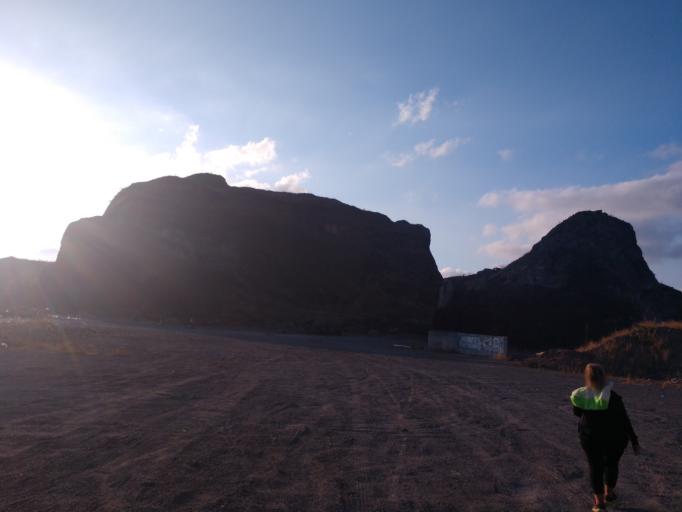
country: MX
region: Nayarit
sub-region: Tepic
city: La Corregidora
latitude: 21.4757
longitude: -104.8118
